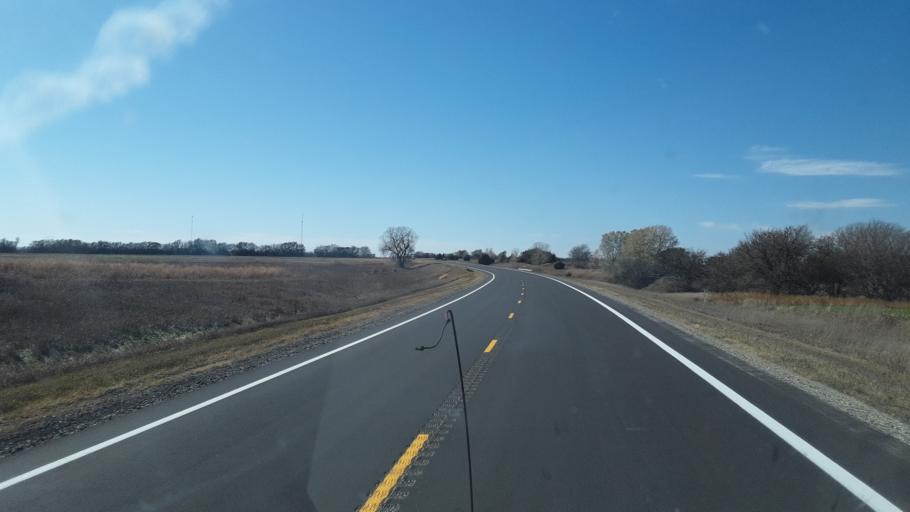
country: US
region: Kansas
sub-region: Rice County
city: Lyons
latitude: 38.3766
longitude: -98.1226
